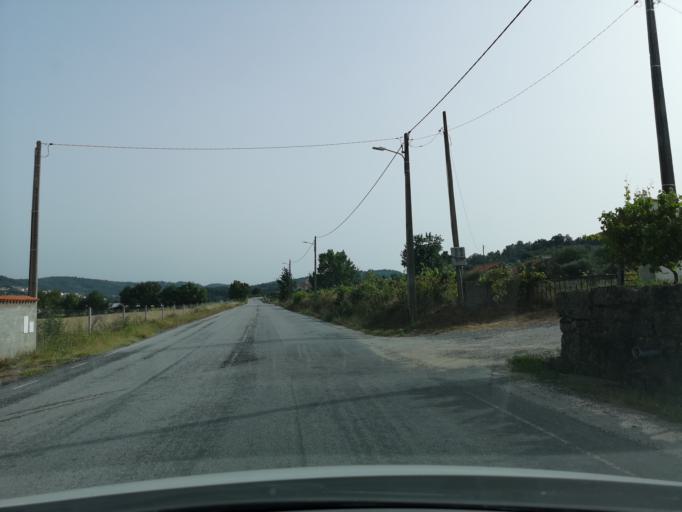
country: PT
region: Castelo Branco
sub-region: Belmonte
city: Belmonte
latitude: 40.3674
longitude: -7.3340
